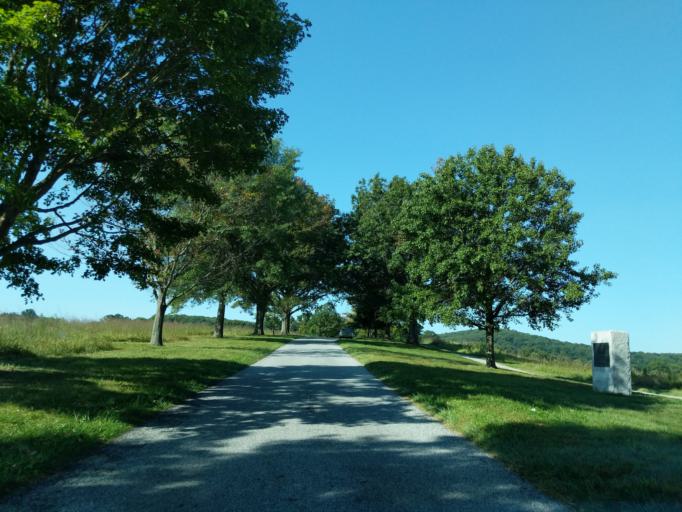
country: US
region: Pennsylvania
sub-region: Chester County
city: Chesterbrook
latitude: 40.0937
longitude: -75.4335
